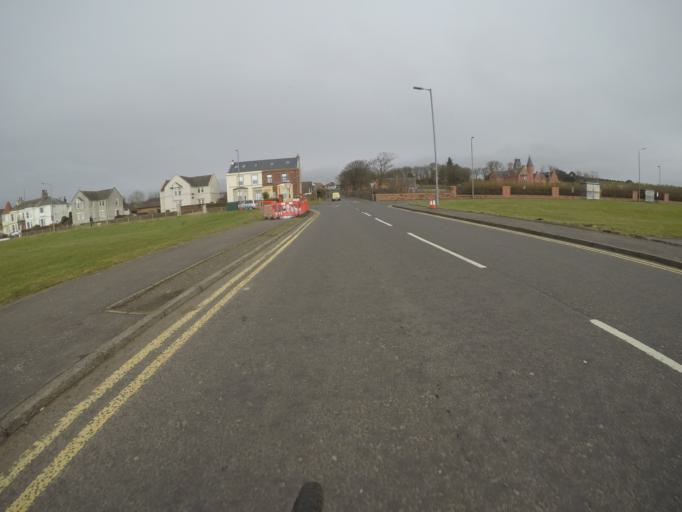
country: GB
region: Scotland
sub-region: North Ayrshire
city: Ardrossan
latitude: 55.6515
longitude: -4.8189
